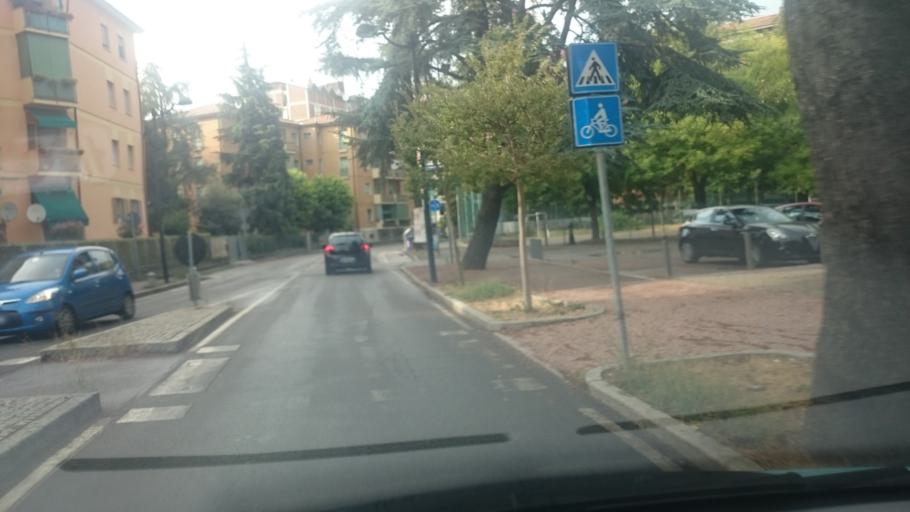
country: IT
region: Emilia-Romagna
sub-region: Provincia di Reggio Emilia
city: Reggio nell'Emilia
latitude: 44.6885
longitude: 10.6376
